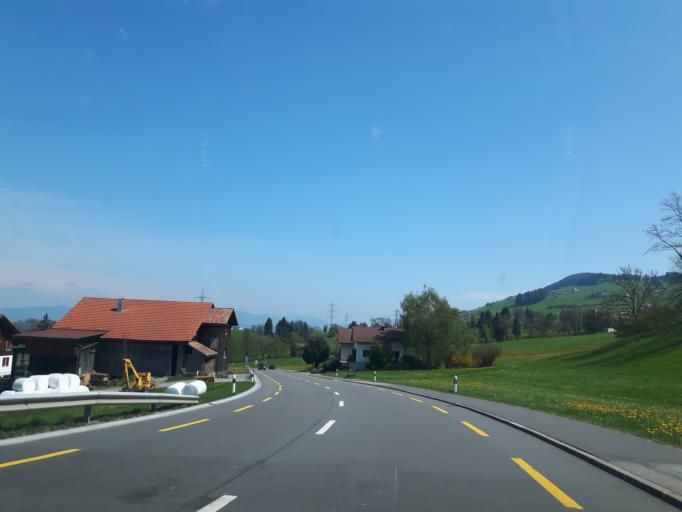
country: CH
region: Schwyz
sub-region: Bezirk Hoefe
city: Schindellegi
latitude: 47.1777
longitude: 8.7187
